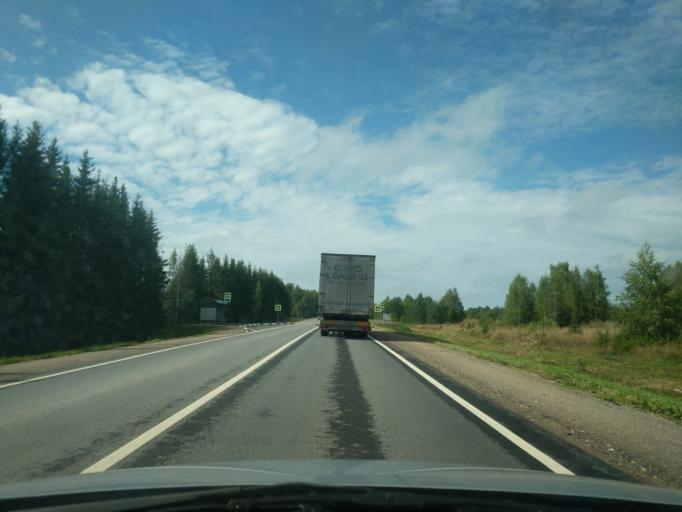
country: RU
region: Kostroma
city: Sudislavl'
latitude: 57.8449
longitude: 41.8254
